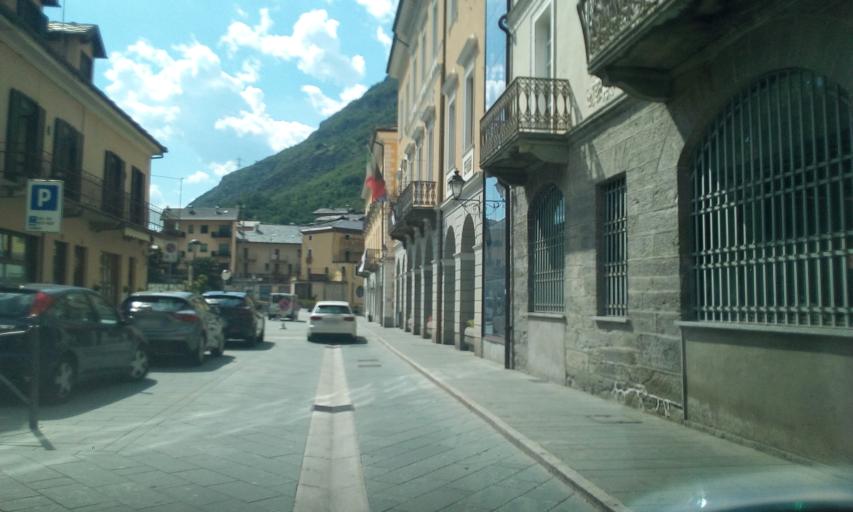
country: IT
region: Aosta Valley
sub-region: Valle d'Aosta
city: Chatillon
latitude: 45.7485
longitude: 7.6116
